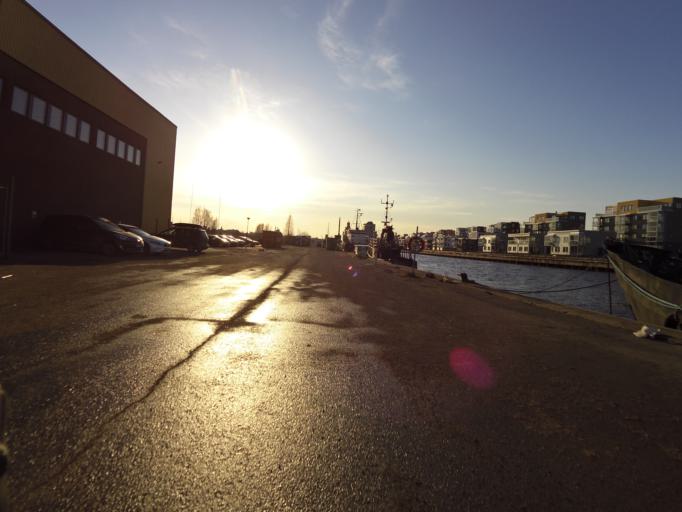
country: SE
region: Gaevleborg
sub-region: Gavle Kommun
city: Gavle
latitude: 60.6793
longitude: 17.1735
